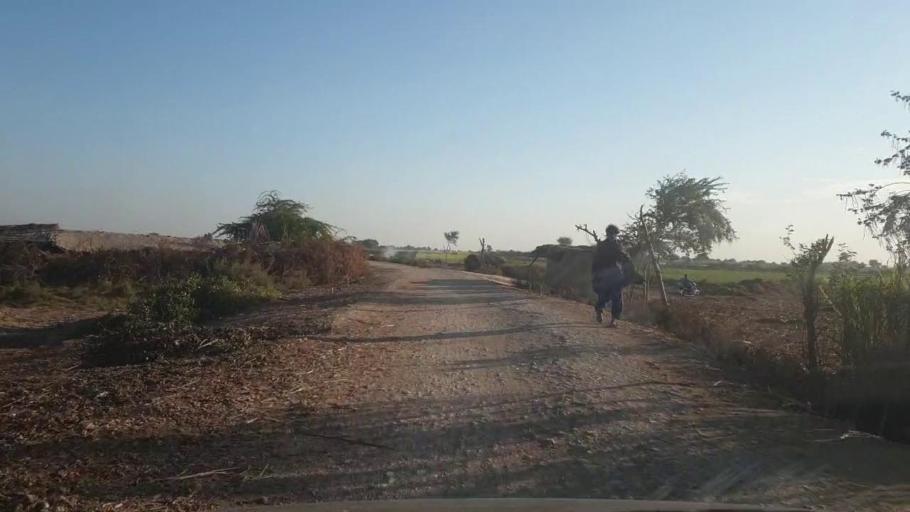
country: PK
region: Sindh
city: Sinjhoro
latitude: 26.0413
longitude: 68.8697
